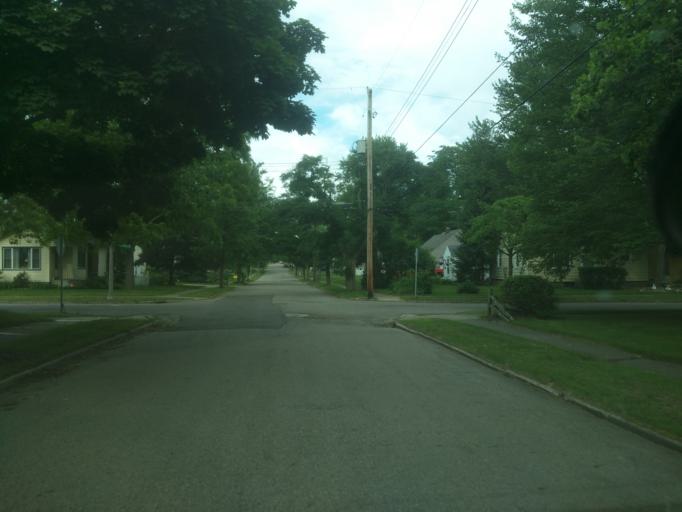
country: US
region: Michigan
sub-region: Ingham County
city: Lansing
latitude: 42.6861
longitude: -84.5456
